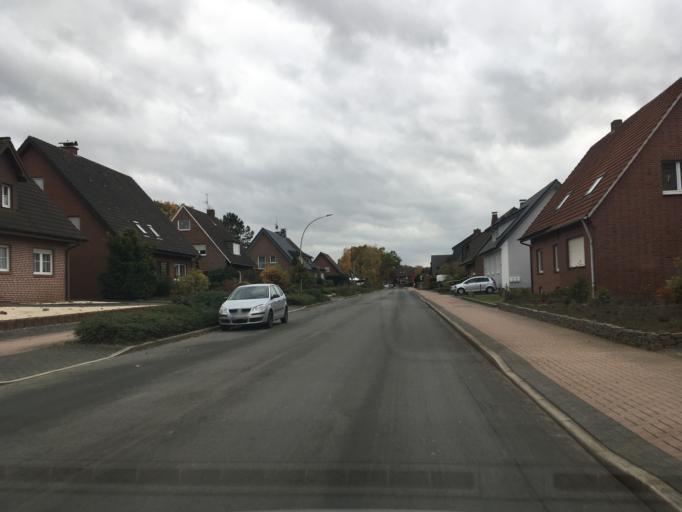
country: DE
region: North Rhine-Westphalia
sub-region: Regierungsbezirk Munster
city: Klein Reken
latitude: 51.8433
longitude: 7.0970
